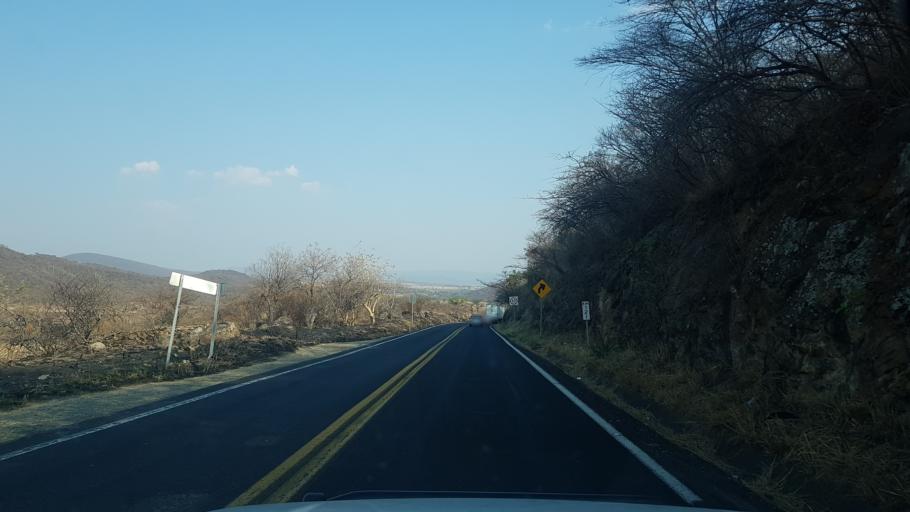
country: MX
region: Puebla
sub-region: Tilapa
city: San Felix Rijo
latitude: 18.6404
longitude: -98.5892
